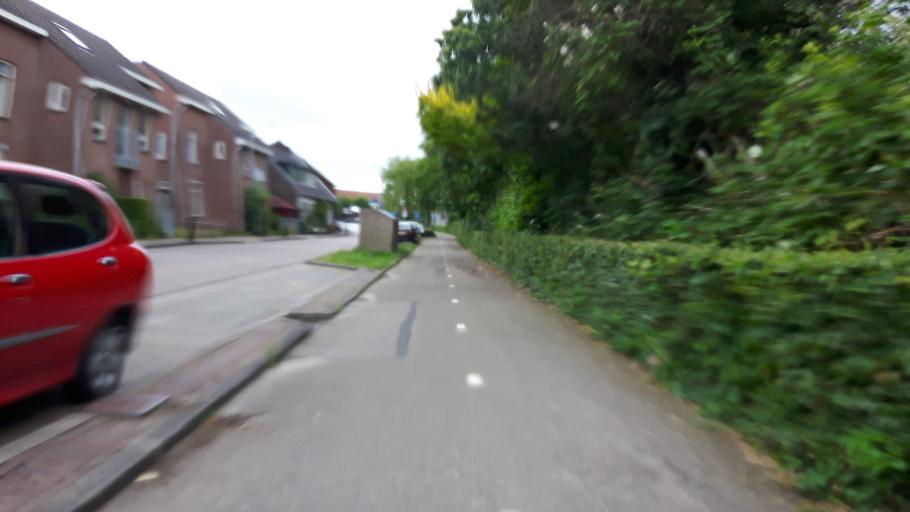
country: NL
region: North Holland
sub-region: Gemeente Wijdemeren
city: Kortenhoef
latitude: 52.2491
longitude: 5.1190
